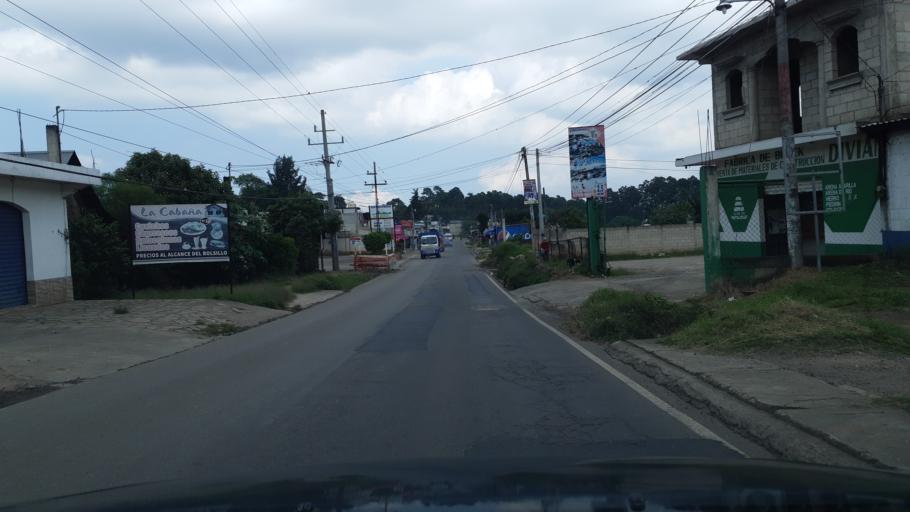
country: GT
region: Chimaltenango
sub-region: Municipio de Chimaltenango
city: Chimaltenango
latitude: 14.6753
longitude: -90.8024
